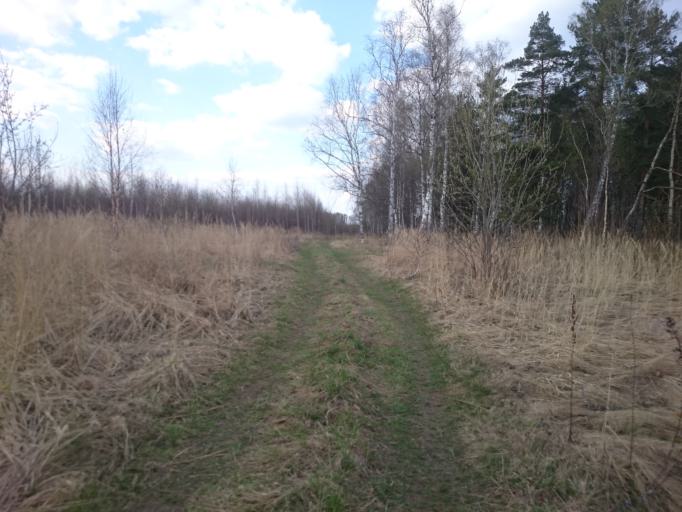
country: RU
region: Moskovskaya
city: Klin
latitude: 56.3978
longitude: 36.6817
